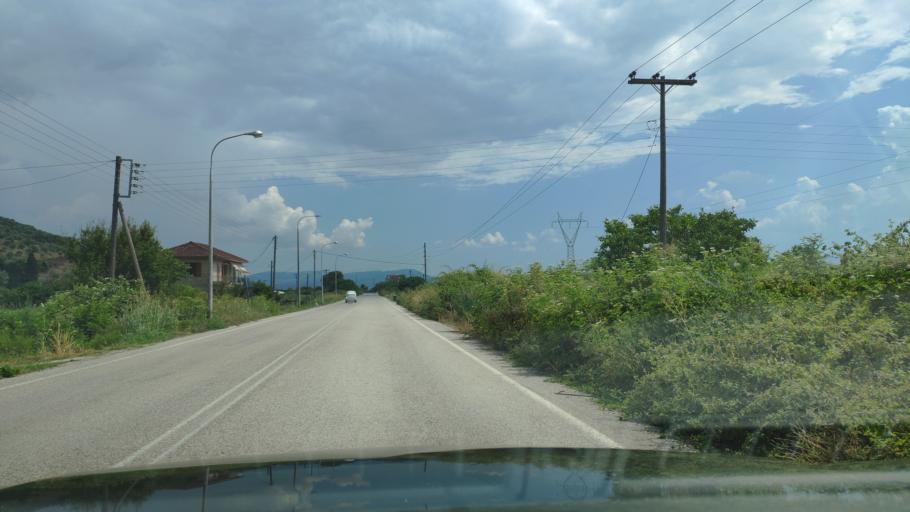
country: GR
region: West Greece
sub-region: Nomos Aitolias kai Akarnanias
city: Krikellos
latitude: 38.9702
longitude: 21.1678
